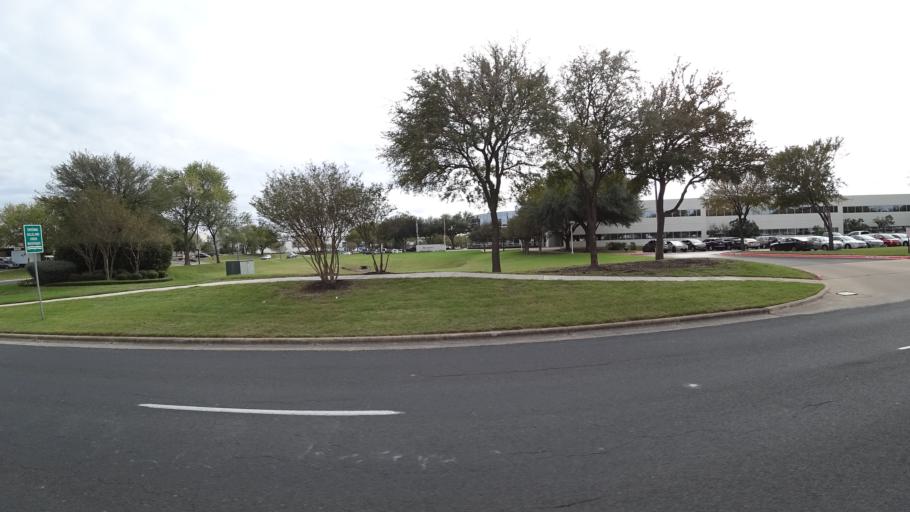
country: US
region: Texas
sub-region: Travis County
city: Wells Branch
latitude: 30.4566
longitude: -97.6726
